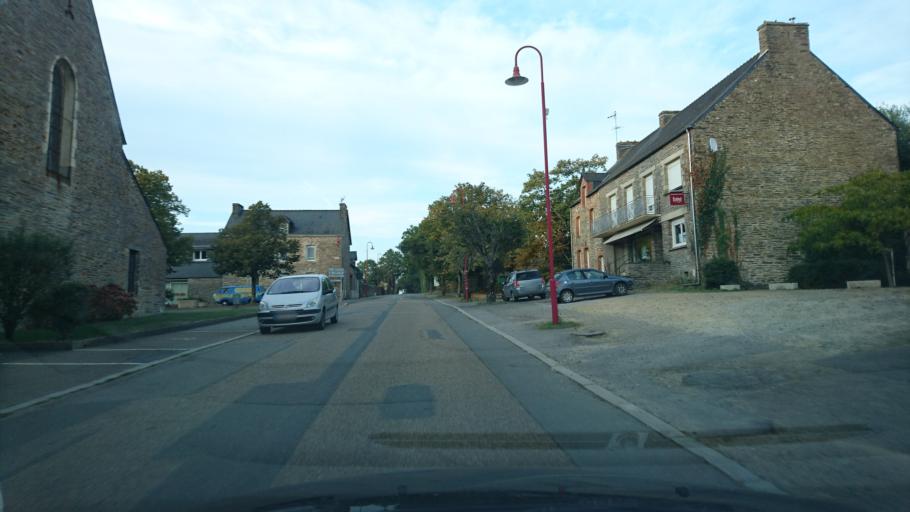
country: FR
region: Brittany
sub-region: Departement d'Ille-et-Vilaine
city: Saint-Just
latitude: 47.7655
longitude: -1.9609
